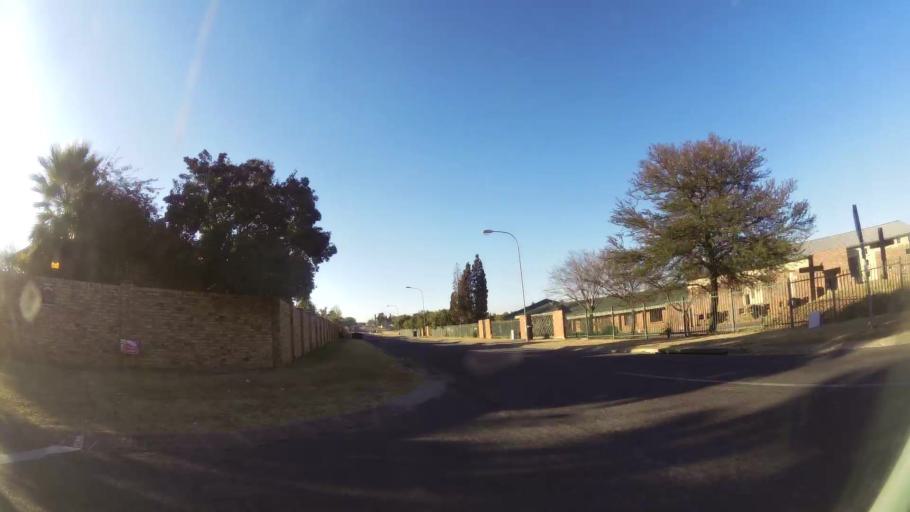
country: ZA
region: Gauteng
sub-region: City of Tshwane Metropolitan Municipality
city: Centurion
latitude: -25.9040
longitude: 28.1417
